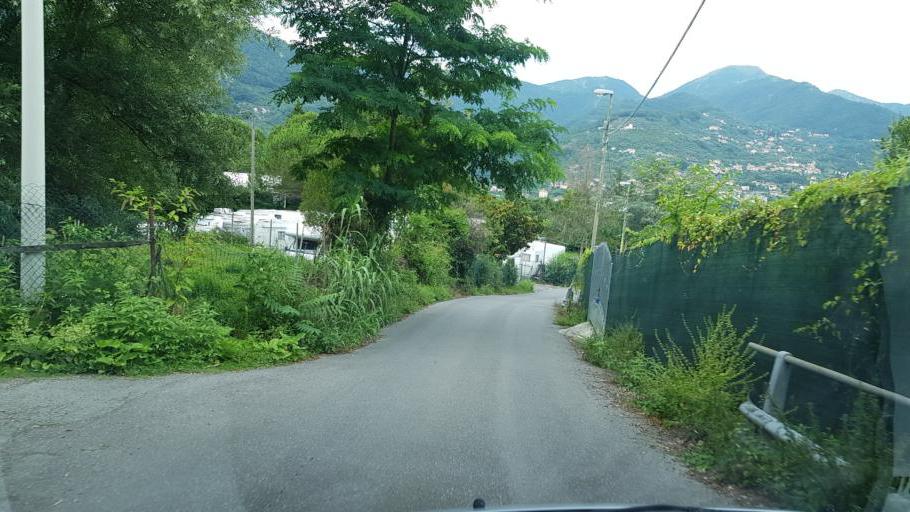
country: IT
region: Liguria
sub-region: Provincia di Genova
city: Piccarello
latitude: 44.4413
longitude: 9.0053
